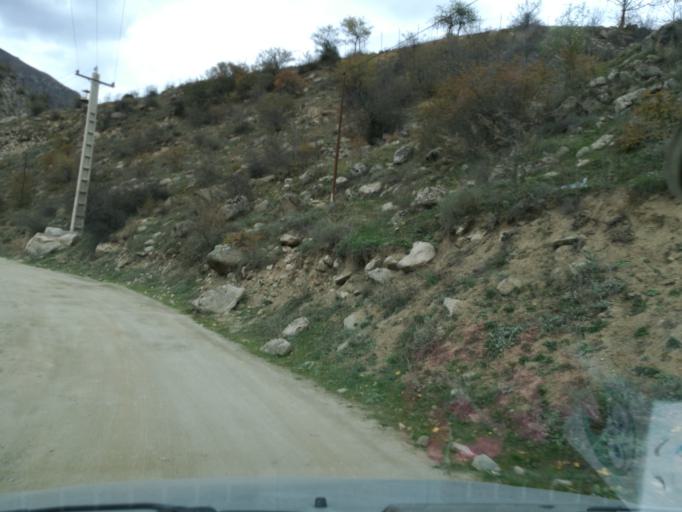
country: IR
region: Mazandaran
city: `Abbasabad
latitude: 36.4358
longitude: 51.0604
